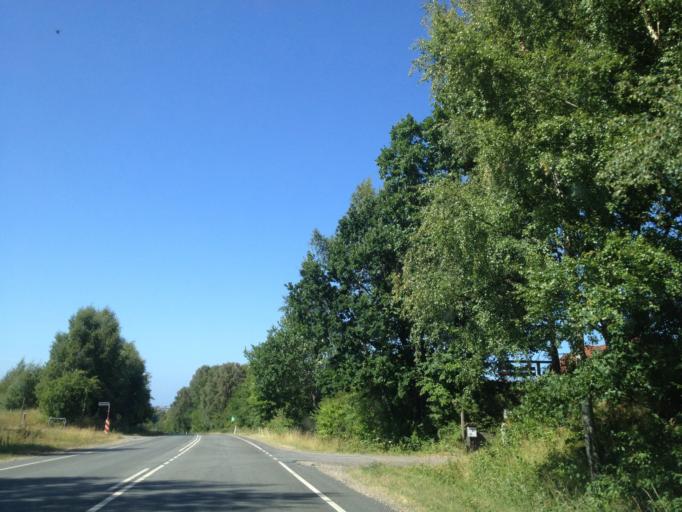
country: DK
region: Capital Region
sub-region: Gribskov Kommune
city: Graested
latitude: 56.0443
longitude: 12.3445
